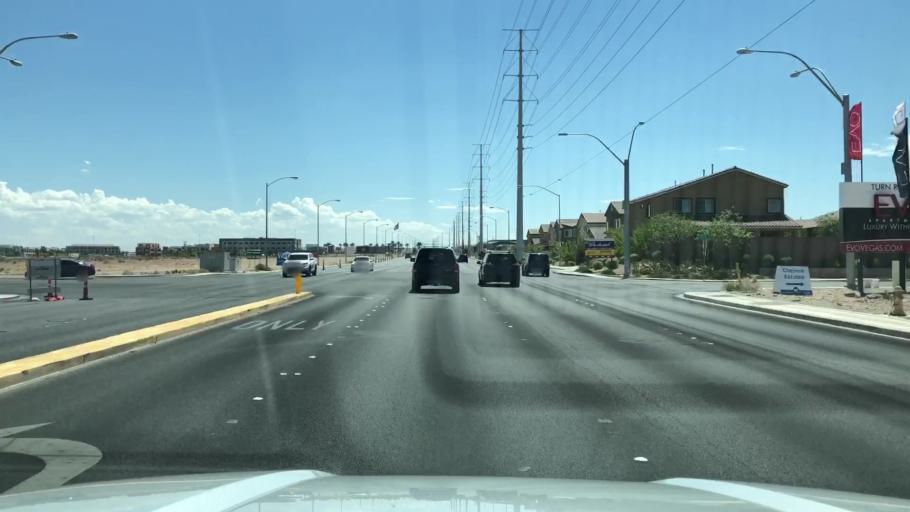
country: US
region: Nevada
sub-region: Clark County
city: Spring Valley
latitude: 36.0782
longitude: -115.2794
